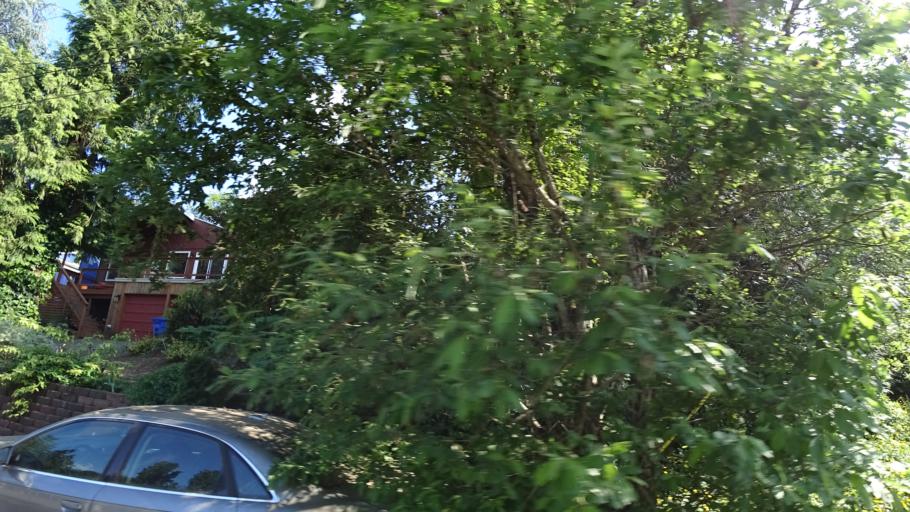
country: US
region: Oregon
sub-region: Washington County
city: Garden Home-Whitford
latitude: 45.4575
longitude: -122.7324
